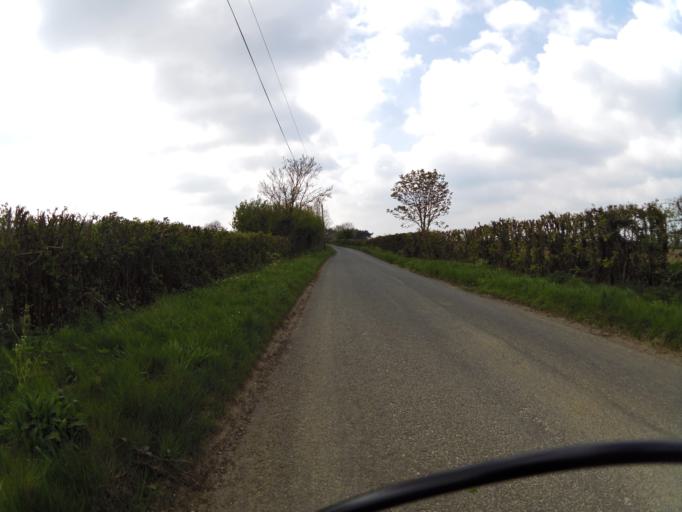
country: GB
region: England
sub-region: Suffolk
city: Hadleigh
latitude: 52.0537
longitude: 0.9121
